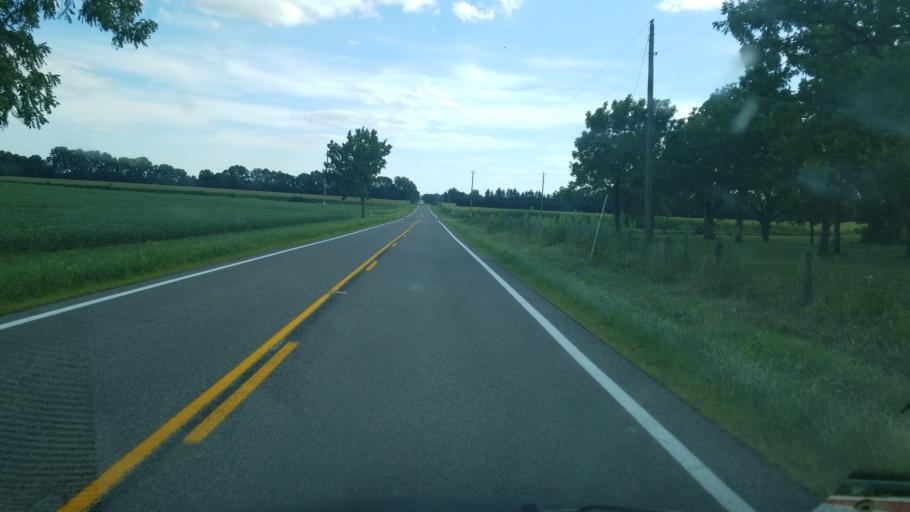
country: US
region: Ohio
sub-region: Champaign County
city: Urbana
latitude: 40.1258
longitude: -83.8358
